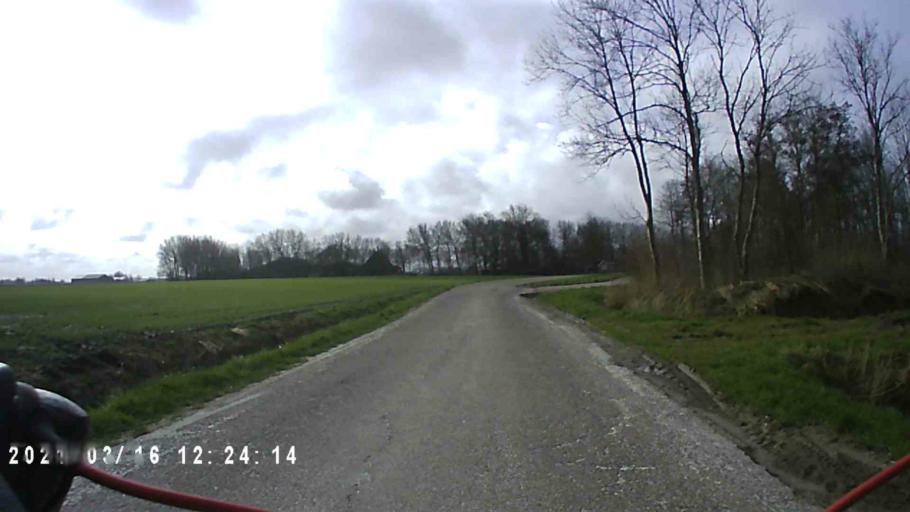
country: NL
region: Friesland
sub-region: Gemeente Ferwerderadiel
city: Hallum
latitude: 53.3003
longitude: 5.7524
